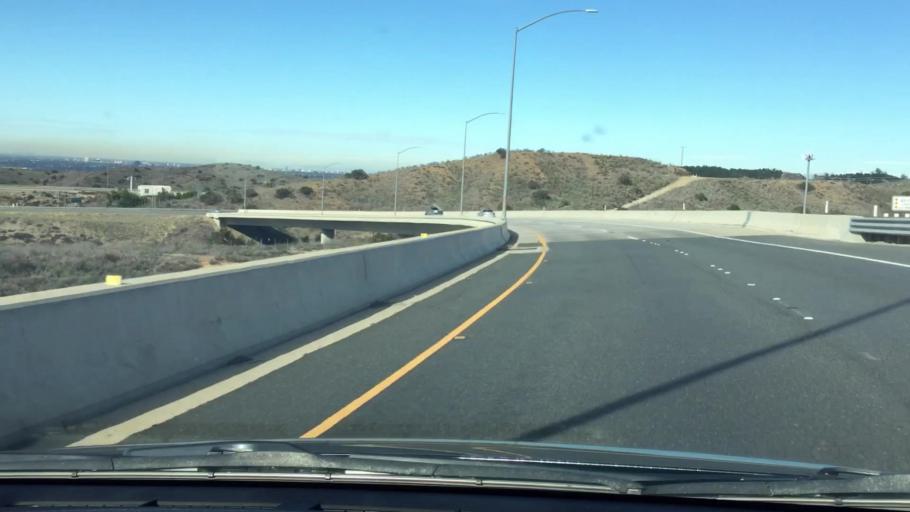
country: US
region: California
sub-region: Orange County
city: Foothill Ranch
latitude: 33.7105
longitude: -117.7189
